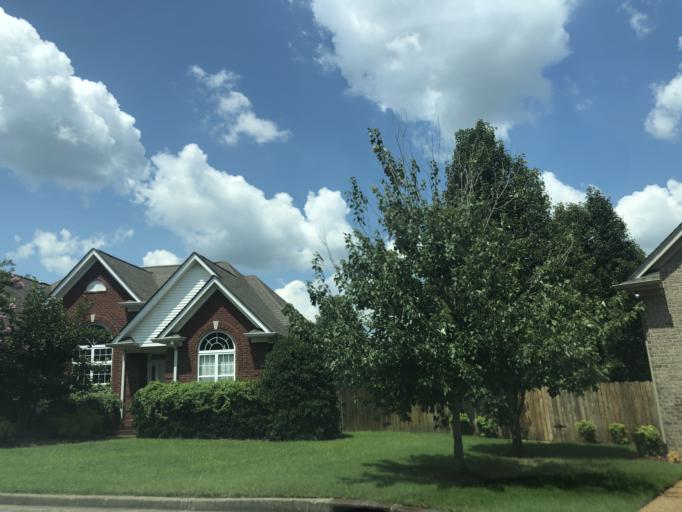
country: US
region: Tennessee
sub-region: Wilson County
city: Green Hill
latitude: 36.1614
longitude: -86.5829
